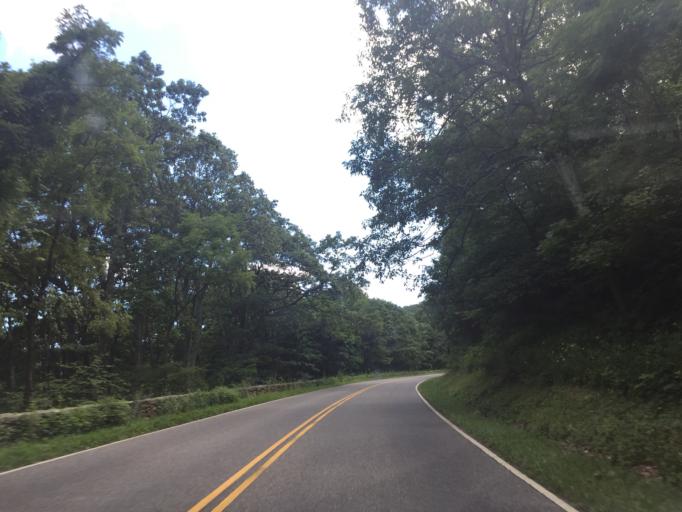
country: US
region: Virginia
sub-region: Page County
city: Luray
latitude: 38.6281
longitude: -78.3220
